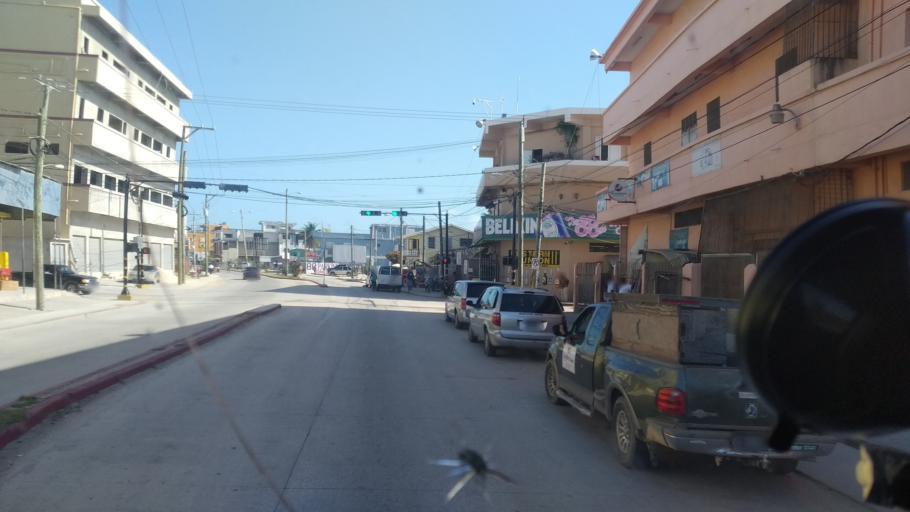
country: BZ
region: Belize
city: Belize City
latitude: 17.4901
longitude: -88.1993
